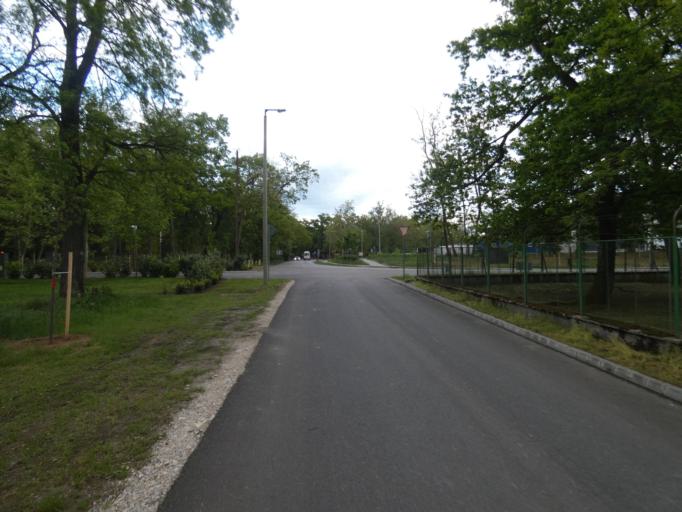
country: HU
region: Szabolcs-Szatmar-Bereg
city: Kotaj
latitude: 48.0092
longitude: 21.7249
